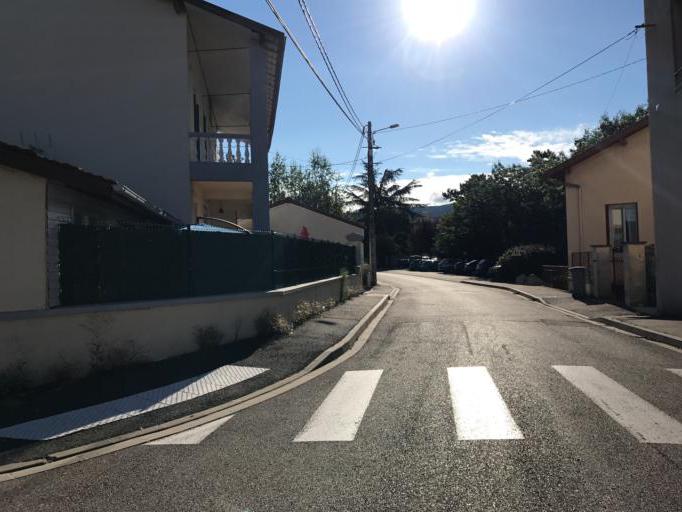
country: FR
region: Rhone-Alpes
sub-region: Departement de l'Ain
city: Amberieu-en-Bugey
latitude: 45.9566
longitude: 5.3437
